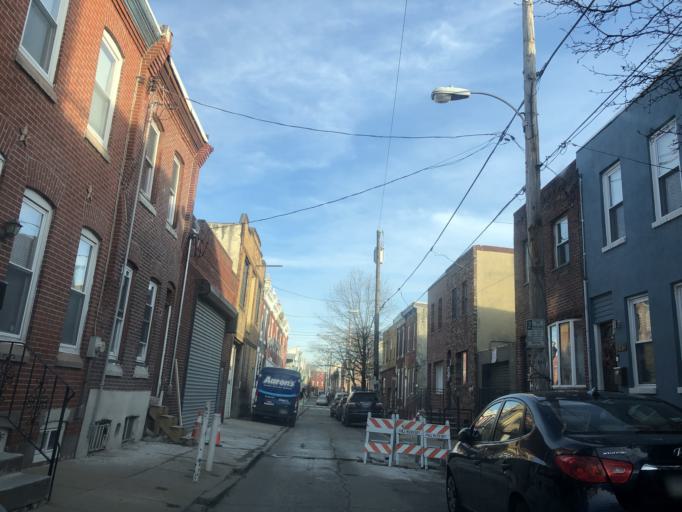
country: US
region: Pennsylvania
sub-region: Philadelphia County
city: Philadelphia
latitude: 39.9234
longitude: -75.1560
